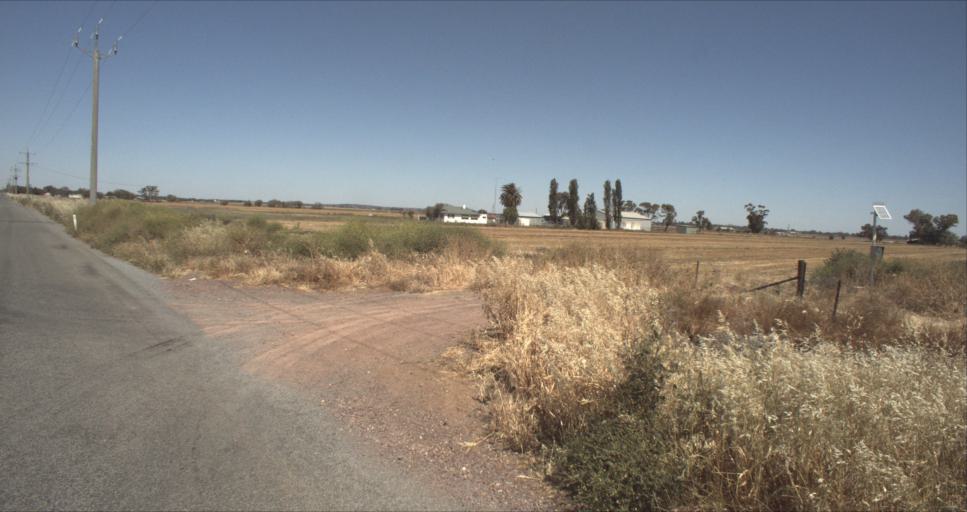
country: AU
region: New South Wales
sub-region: Leeton
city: Leeton
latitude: -34.5111
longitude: 146.4277
